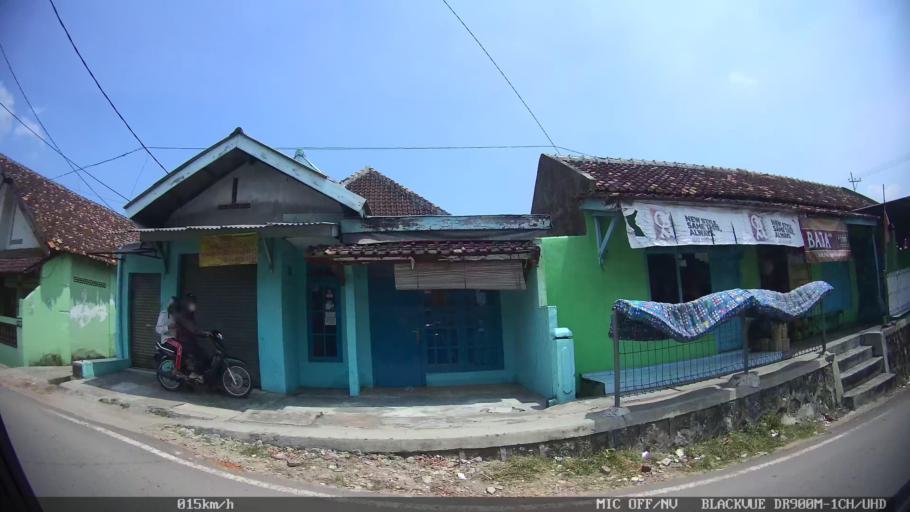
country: ID
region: Lampung
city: Kedaton
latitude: -5.4038
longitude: 105.2613
